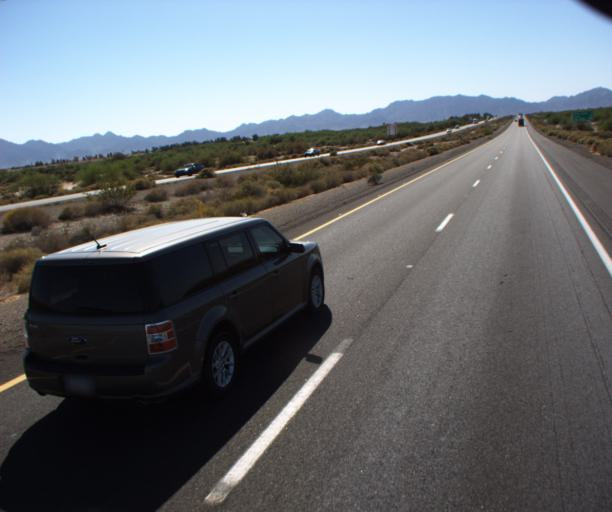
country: US
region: Arizona
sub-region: Yuma County
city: Wellton
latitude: 32.6582
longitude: -114.1585
